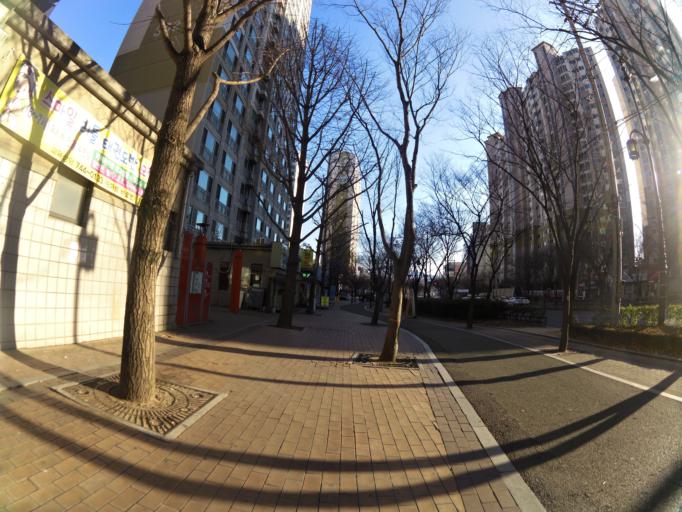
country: KR
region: Daegu
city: Daegu
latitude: 35.8693
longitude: 128.6374
